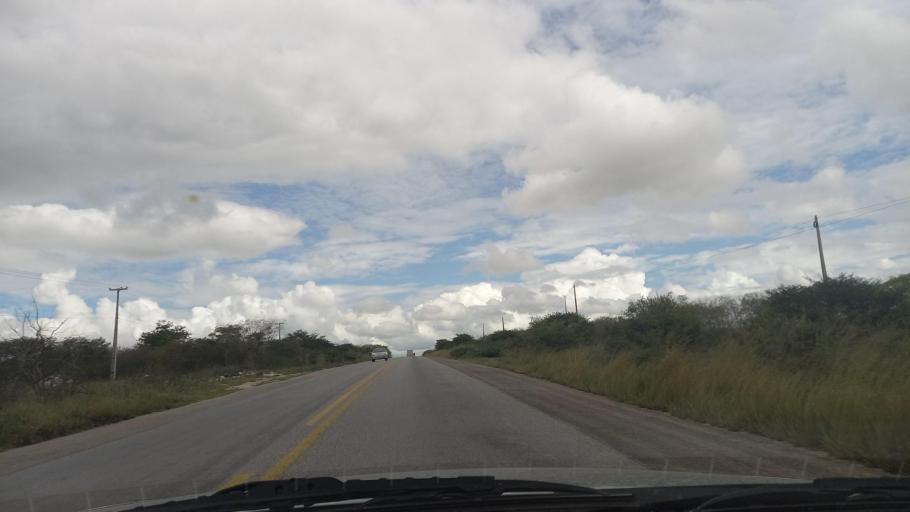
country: BR
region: Pernambuco
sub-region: Cachoeirinha
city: Cachoeirinha
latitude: -8.3584
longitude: -36.1721
